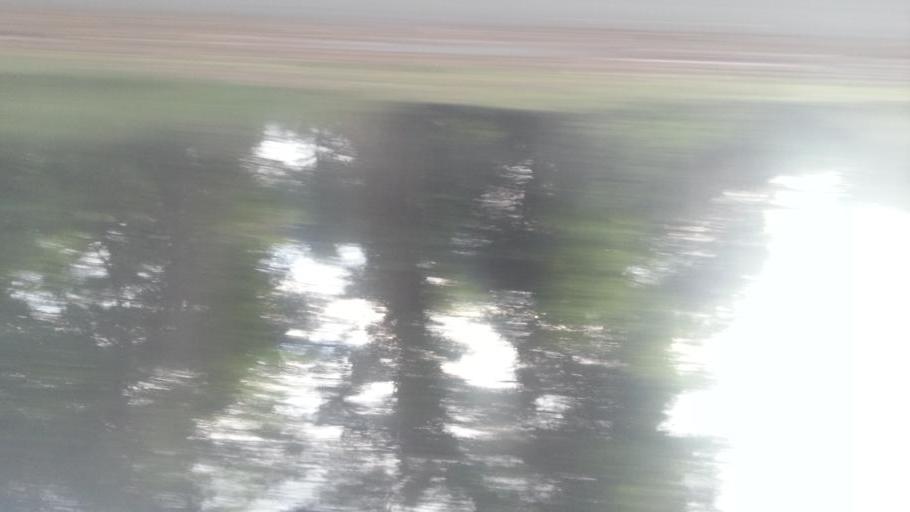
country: AU
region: New South Wales
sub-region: Wollongong
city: Mount Ousley
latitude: -34.3841
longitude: 150.8557
